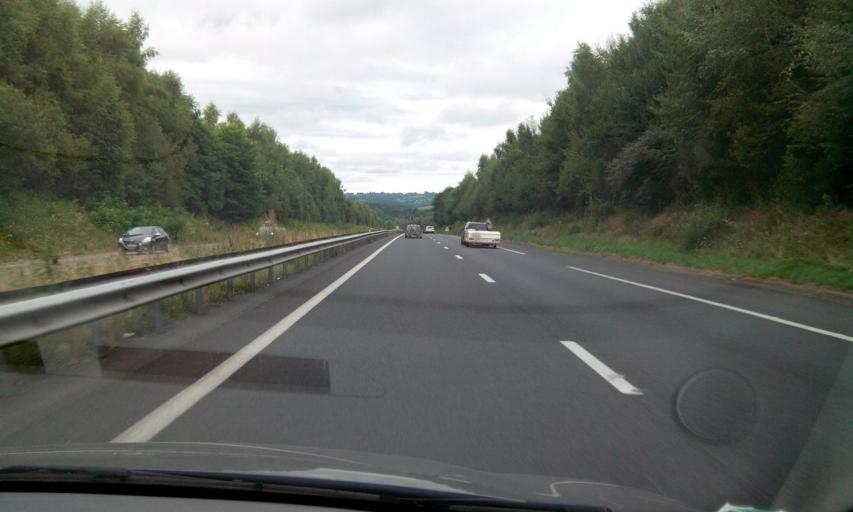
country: FR
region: Limousin
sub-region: Departement de la Correze
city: Uzerche
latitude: 45.3977
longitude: 1.5661
